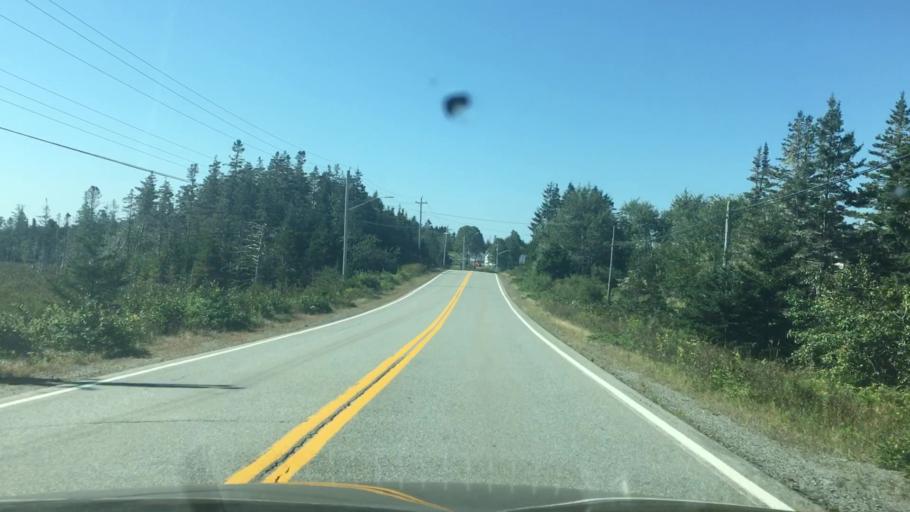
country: CA
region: Nova Scotia
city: New Glasgow
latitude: 44.8068
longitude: -62.6921
